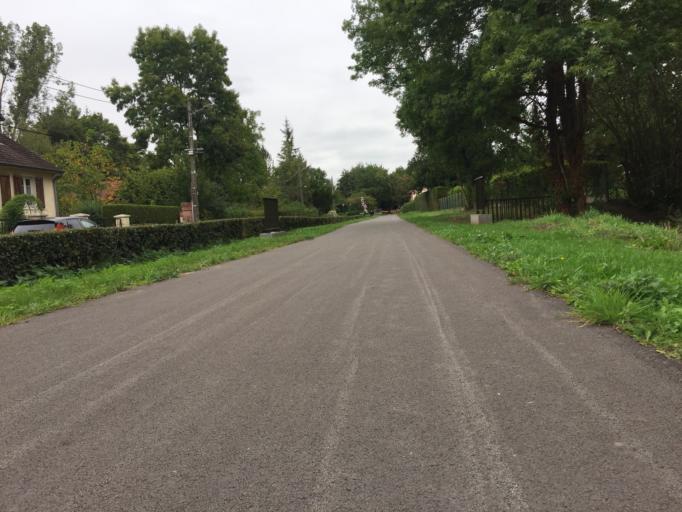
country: FR
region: Picardie
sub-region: Departement de l'Oise
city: Saint-Paul
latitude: 49.4068
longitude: 2.0092
